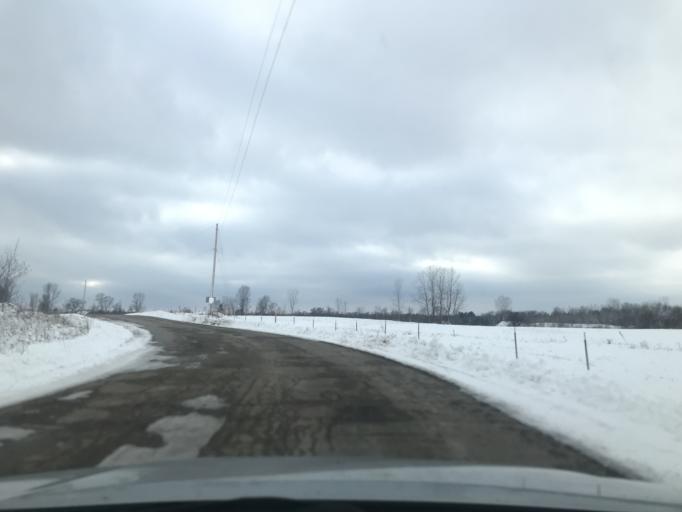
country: US
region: Wisconsin
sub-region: Oconto County
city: Oconto
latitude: 44.9322
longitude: -87.9906
